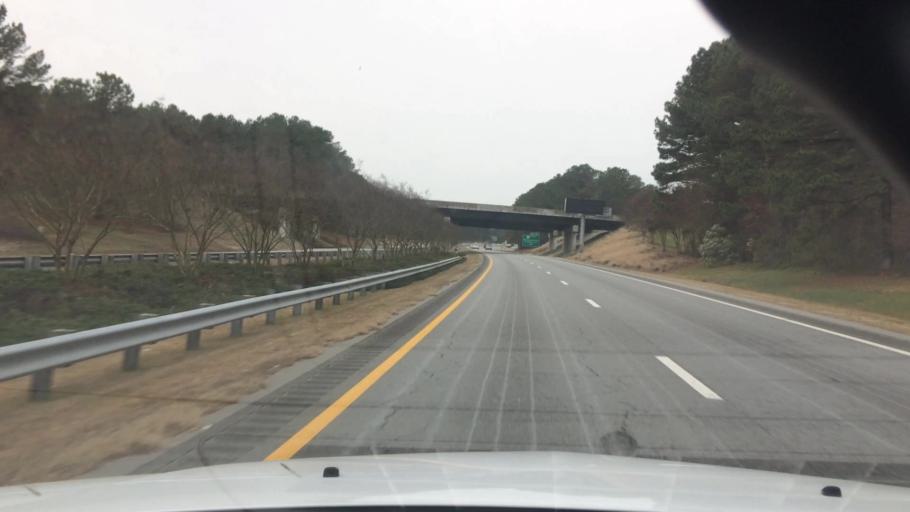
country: US
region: North Carolina
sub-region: Nash County
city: Rocky Mount
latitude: 35.9706
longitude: -77.8324
